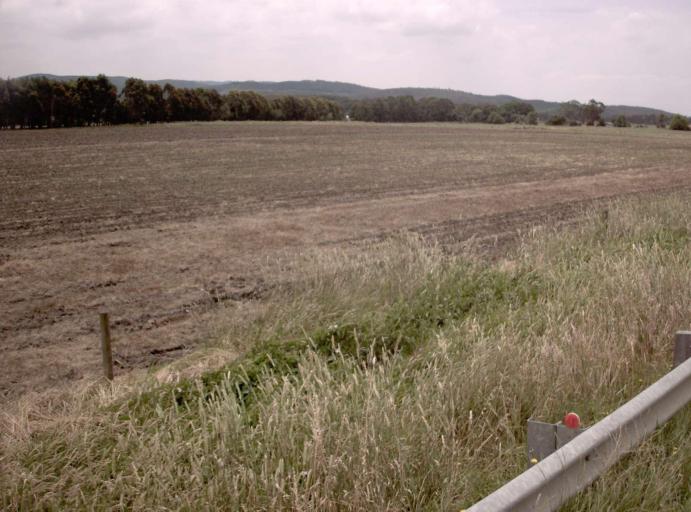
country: AU
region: Victoria
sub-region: Latrobe
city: Traralgon
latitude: -38.5038
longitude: 146.6660
